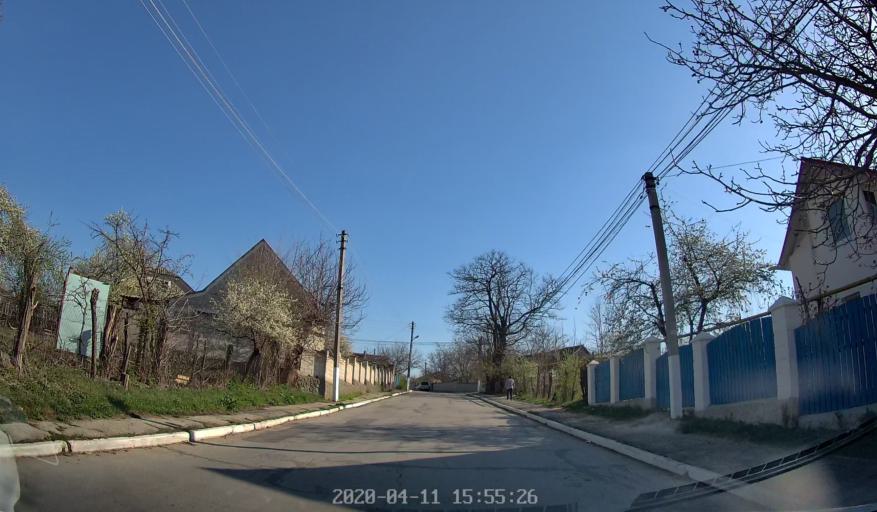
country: MD
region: Chisinau
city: Vadul lui Voda
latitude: 47.0960
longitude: 29.1772
